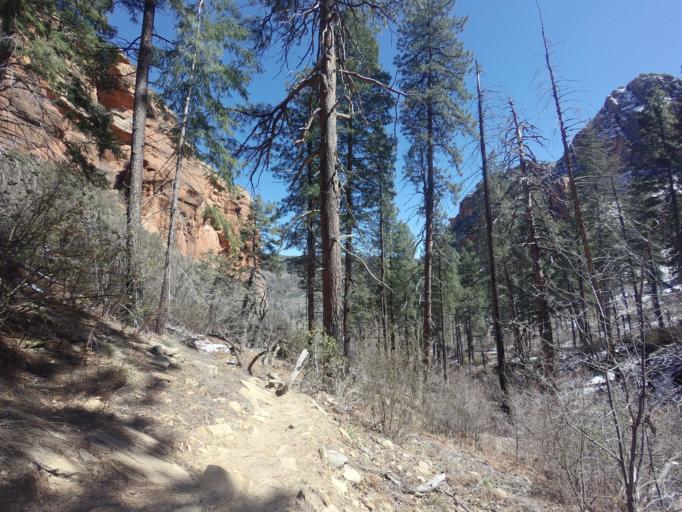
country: US
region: Arizona
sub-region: Coconino County
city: Sedona
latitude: 34.9336
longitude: -111.7571
